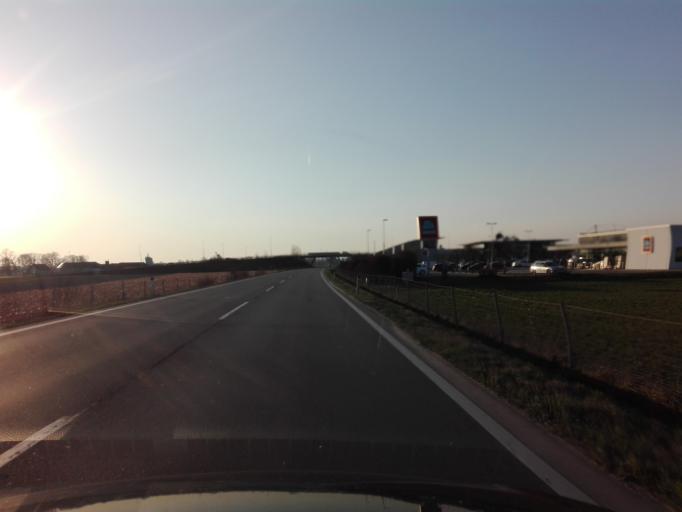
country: AT
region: Upper Austria
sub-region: Politischer Bezirk Perg
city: Perg
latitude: 48.2355
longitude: 14.6272
